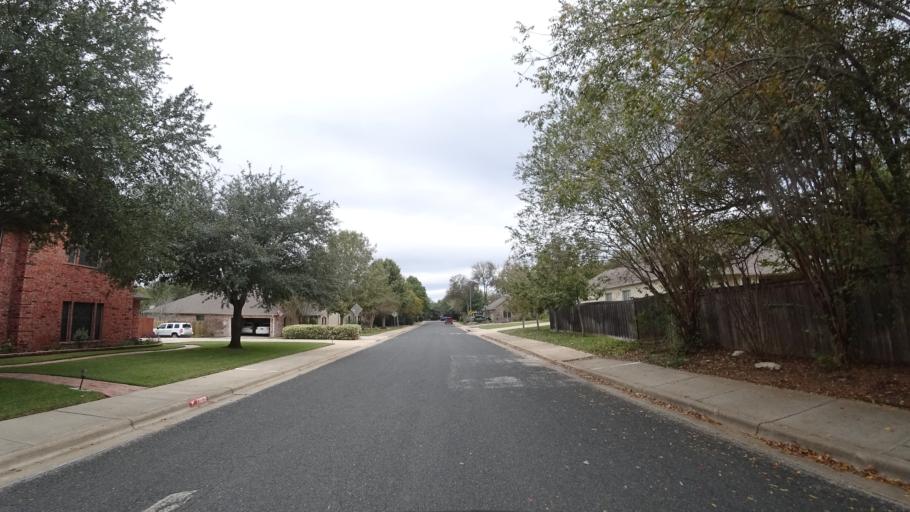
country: US
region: Texas
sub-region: Travis County
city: Shady Hollow
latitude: 30.1569
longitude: -97.8541
